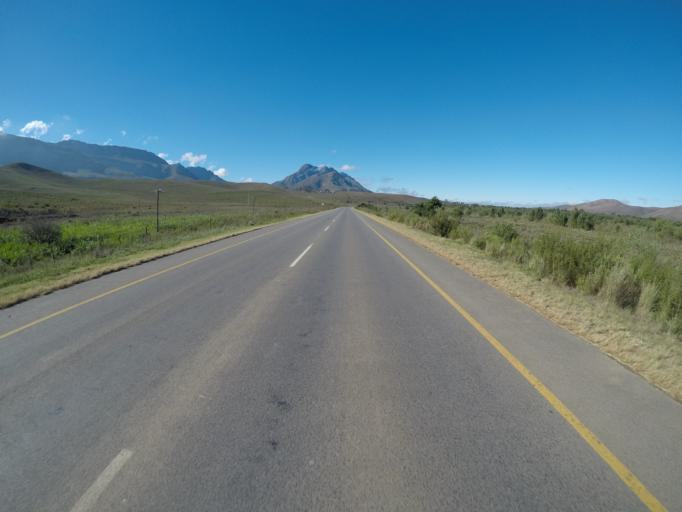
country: ZA
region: Western Cape
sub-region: Overberg District Municipality
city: Caledon
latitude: -34.0491
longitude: 19.5778
